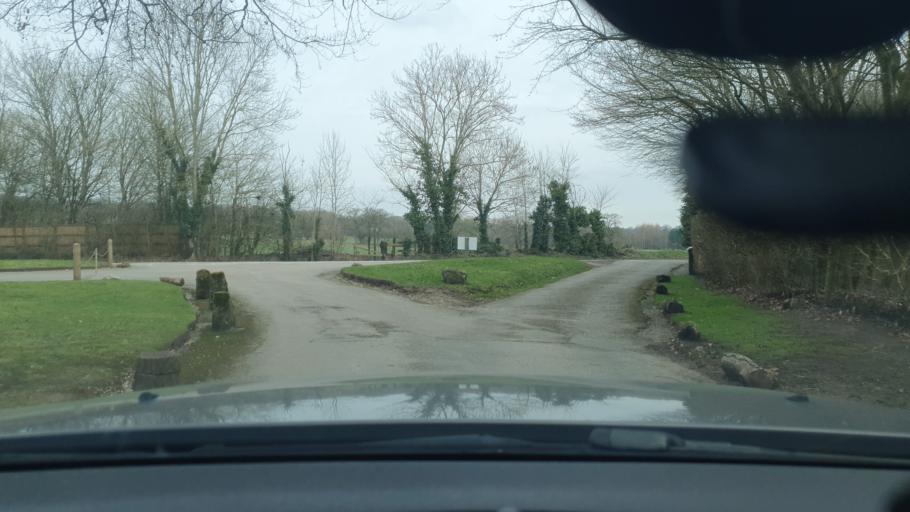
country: GB
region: England
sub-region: Wiltshire
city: Ramsbury
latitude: 51.4395
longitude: -1.6223
